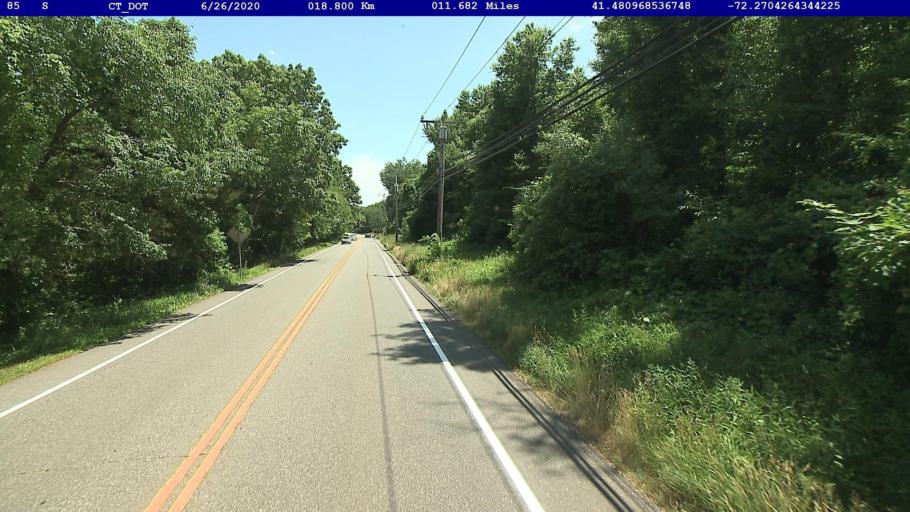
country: US
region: Connecticut
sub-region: New London County
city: Colchester
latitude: 41.4810
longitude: -72.2705
